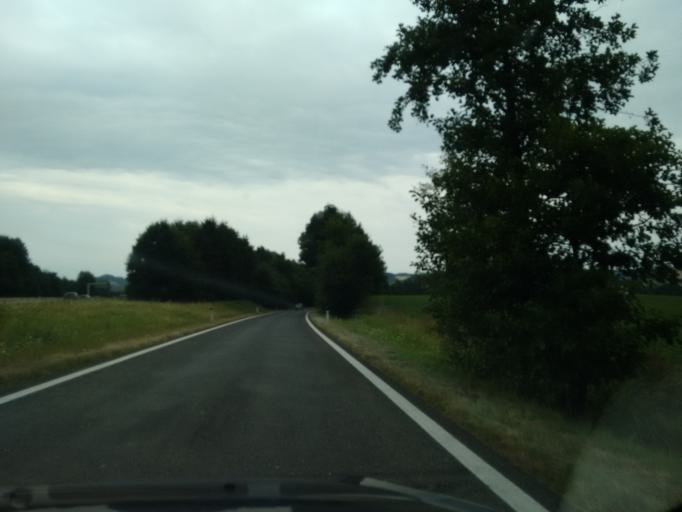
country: AT
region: Upper Austria
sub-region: Politischer Bezirk Grieskirchen
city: Bad Schallerbach
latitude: 48.1895
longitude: 13.9316
